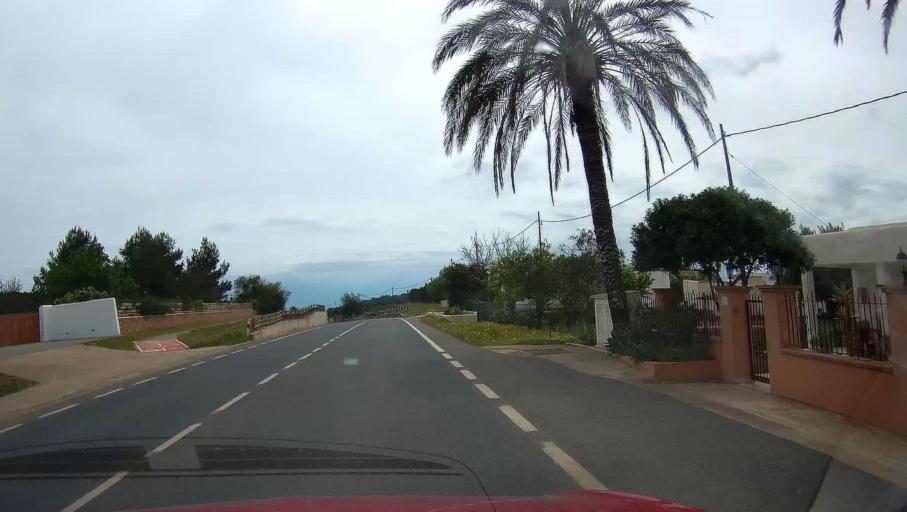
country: ES
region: Balearic Islands
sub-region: Illes Balears
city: Sant Joan de Labritja
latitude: 39.0170
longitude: 1.4272
